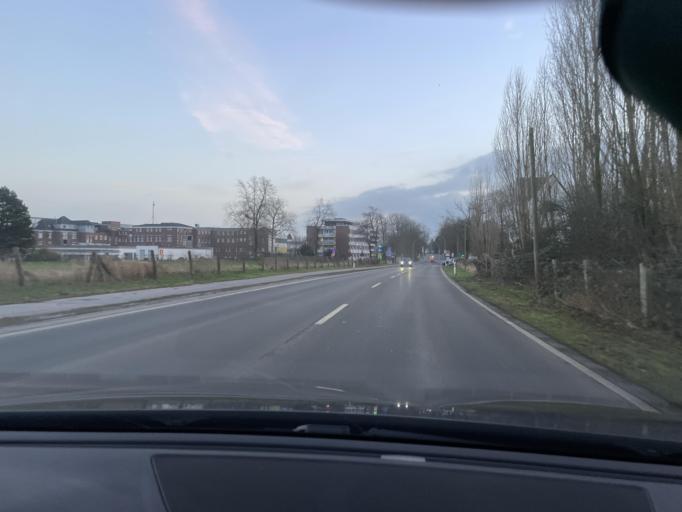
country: DE
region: North Rhine-Westphalia
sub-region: Regierungsbezirk Dusseldorf
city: Viersen
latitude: 51.2212
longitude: 6.4169
